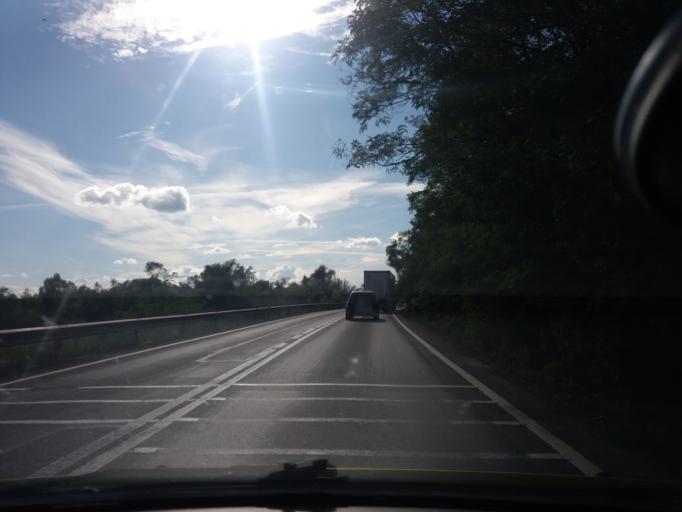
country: RO
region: Arad
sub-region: Comuna Bata
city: Bata
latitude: 46.0352
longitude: 22.0691
